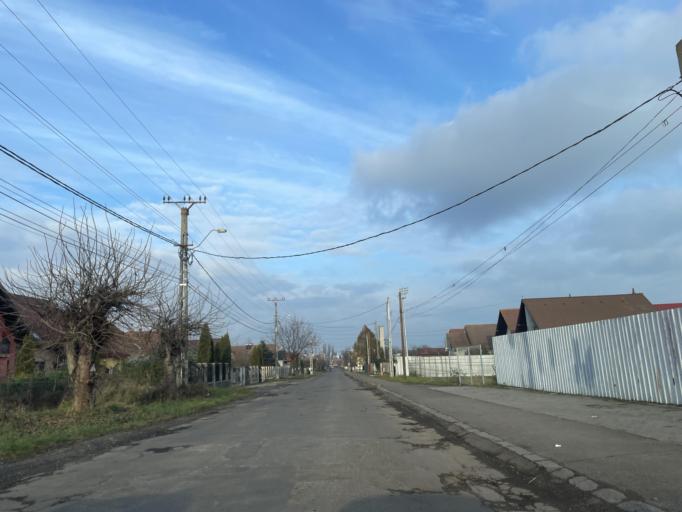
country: RO
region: Mures
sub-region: Municipiul Reghin
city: Reghin
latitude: 46.7650
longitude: 24.6940
